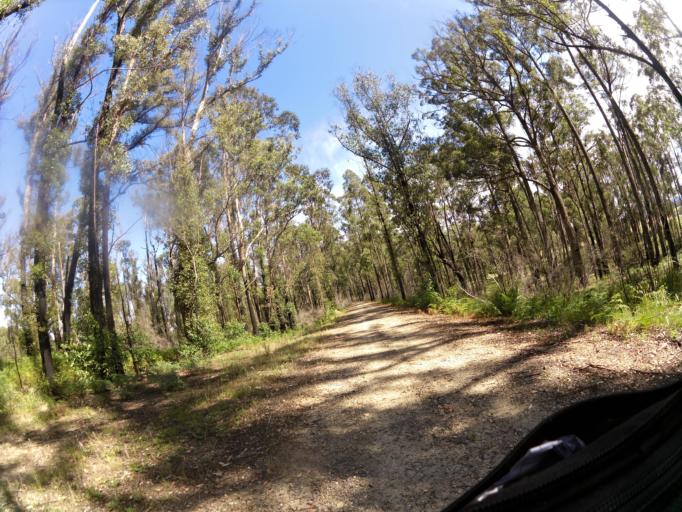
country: AU
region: Victoria
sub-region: East Gippsland
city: Lakes Entrance
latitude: -37.7275
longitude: 148.1613
